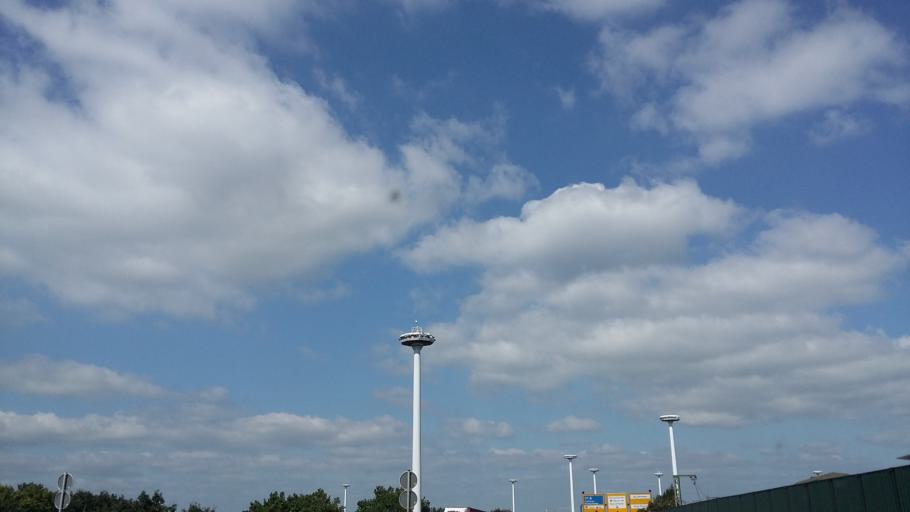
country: DE
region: Bremen
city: Bremen
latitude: 53.0840
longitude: 8.7934
